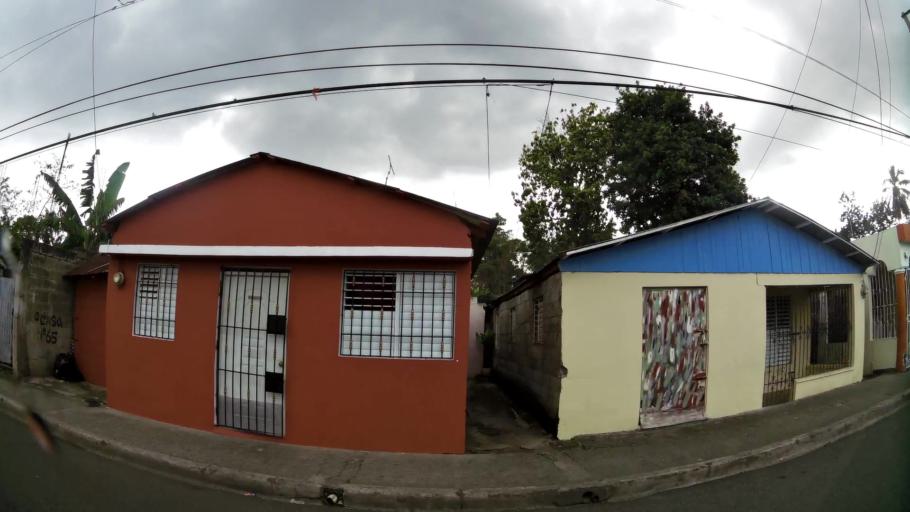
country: DO
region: Monsenor Nouel
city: Bonao
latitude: 18.9486
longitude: -70.4069
